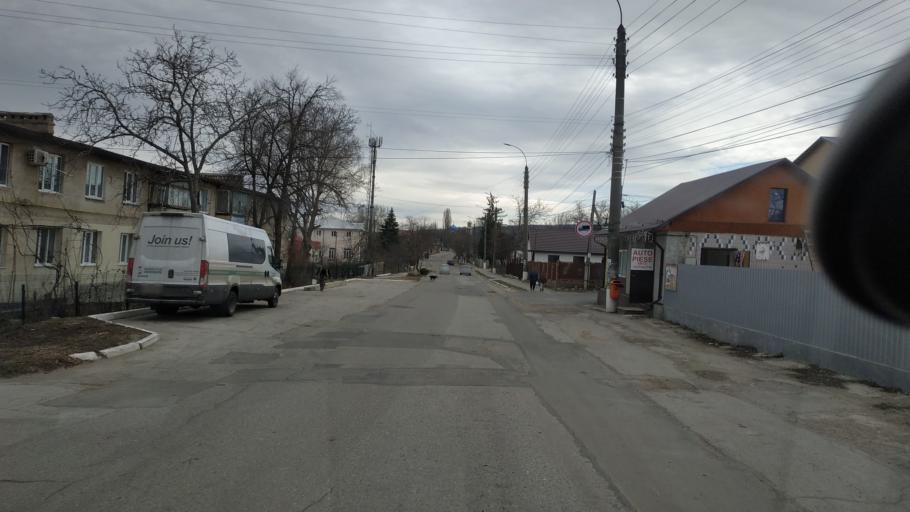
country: MD
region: Chisinau
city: Vadul lui Voda
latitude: 47.0929
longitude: 29.0744
